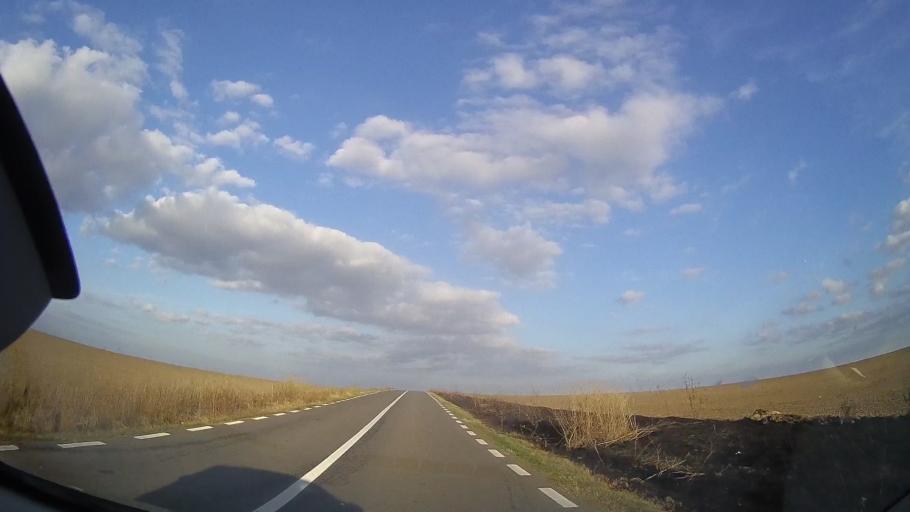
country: RO
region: Constanta
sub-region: Comuna Independenta
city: Independenta
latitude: 43.9433
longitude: 28.0563
